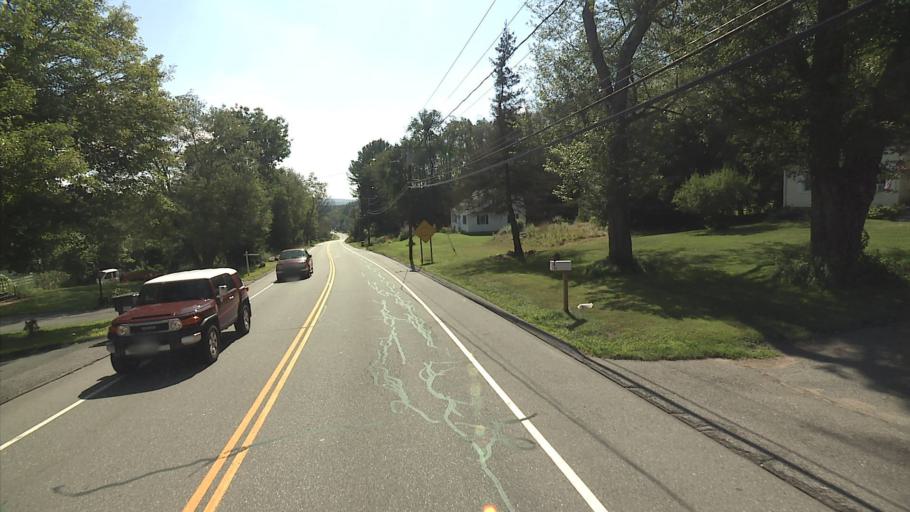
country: US
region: Connecticut
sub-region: Tolland County
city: Crystal Lake
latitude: 41.9716
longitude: -72.3648
